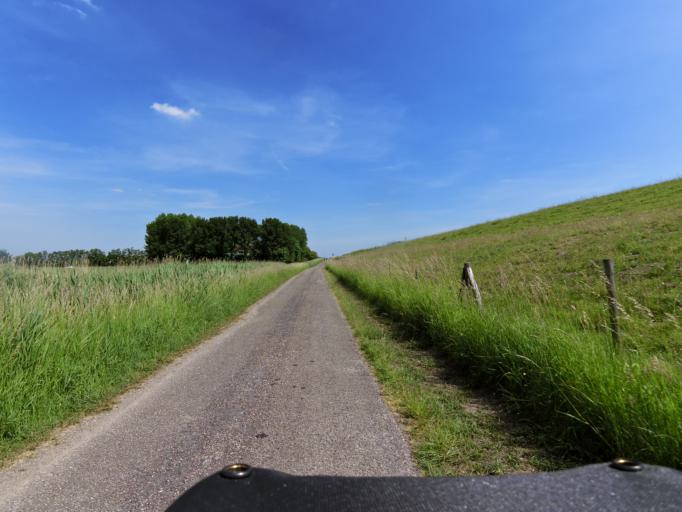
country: NL
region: South Holland
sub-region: Gemeente Spijkenisse
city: Spijkenisse
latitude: 51.7573
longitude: 4.2996
